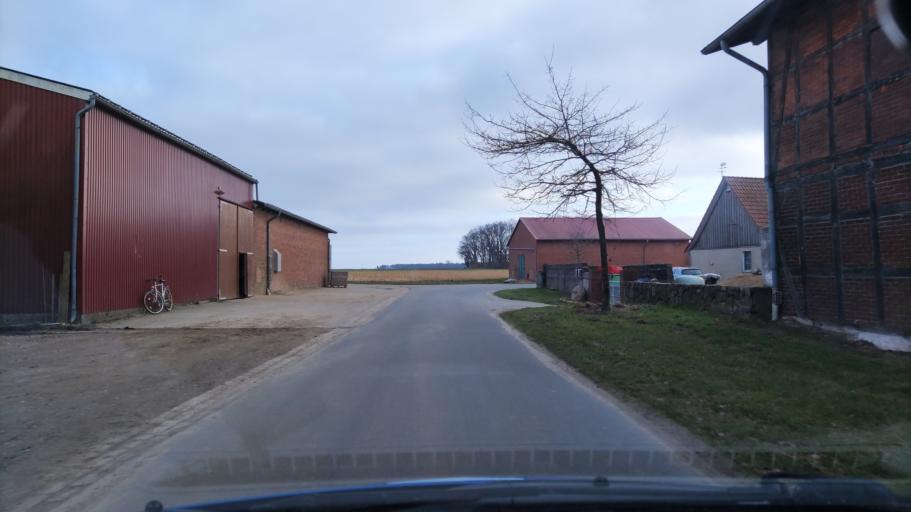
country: DE
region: Lower Saxony
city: Gerdau
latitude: 52.9567
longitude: 10.4317
